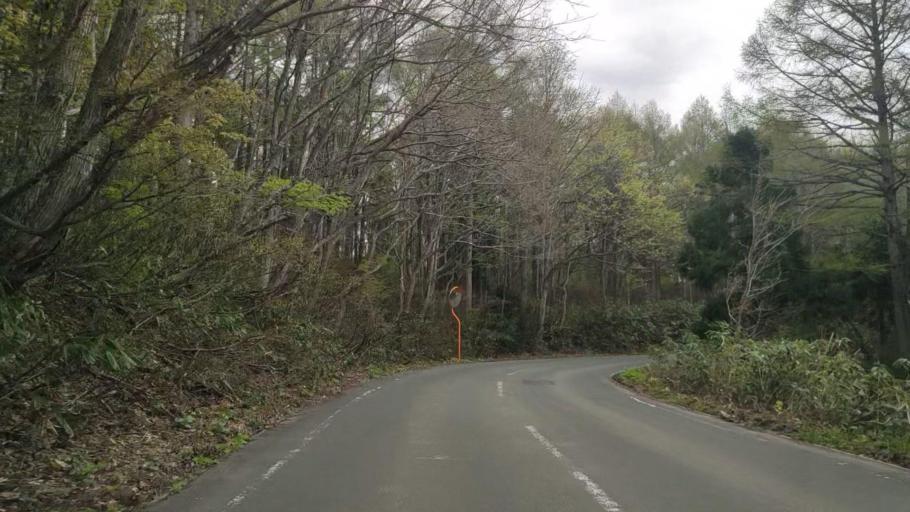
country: JP
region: Aomori
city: Aomori Shi
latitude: 40.7305
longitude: 140.8444
